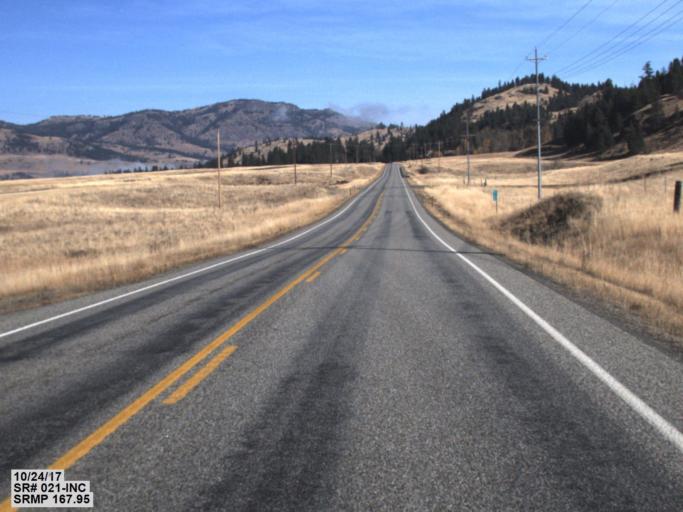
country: US
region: Washington
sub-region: Ferry County
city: Republic
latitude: 48.7150
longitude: -118.6551
